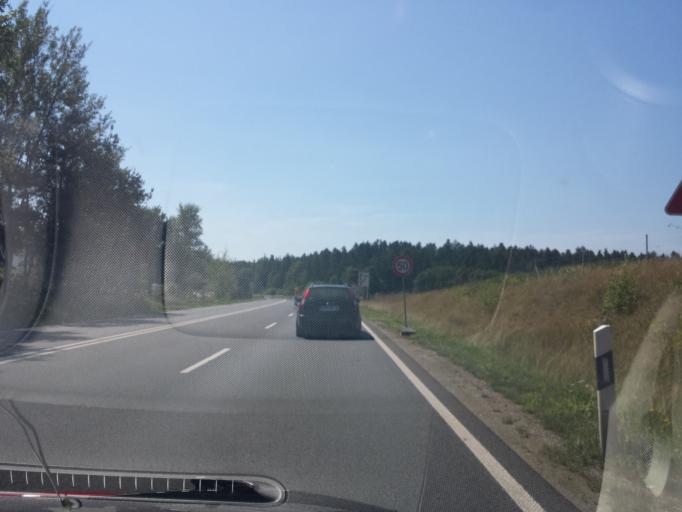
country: DE
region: Bavaria
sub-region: Upper Palatinate
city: Weiding
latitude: 49.2650
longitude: 12.7493
